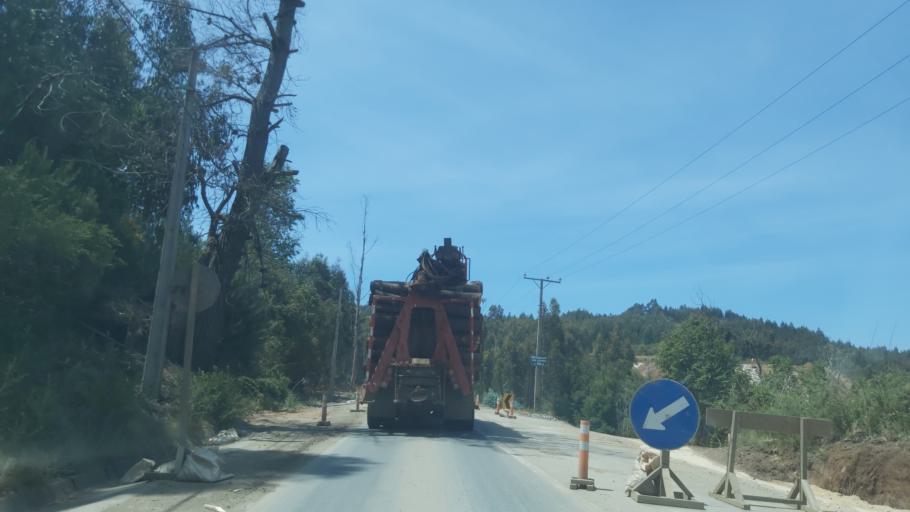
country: CL
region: Maule
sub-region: Provincia de Talca
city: Constitucion
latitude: -35.4460
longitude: -72.4673
